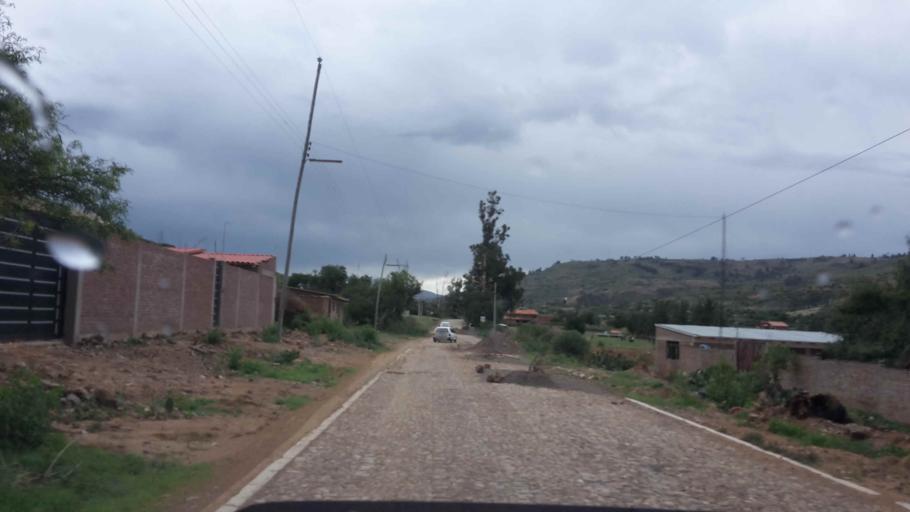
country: BO
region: Cochabamba
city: Cochabamba
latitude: -17.5460
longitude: -66.1873
